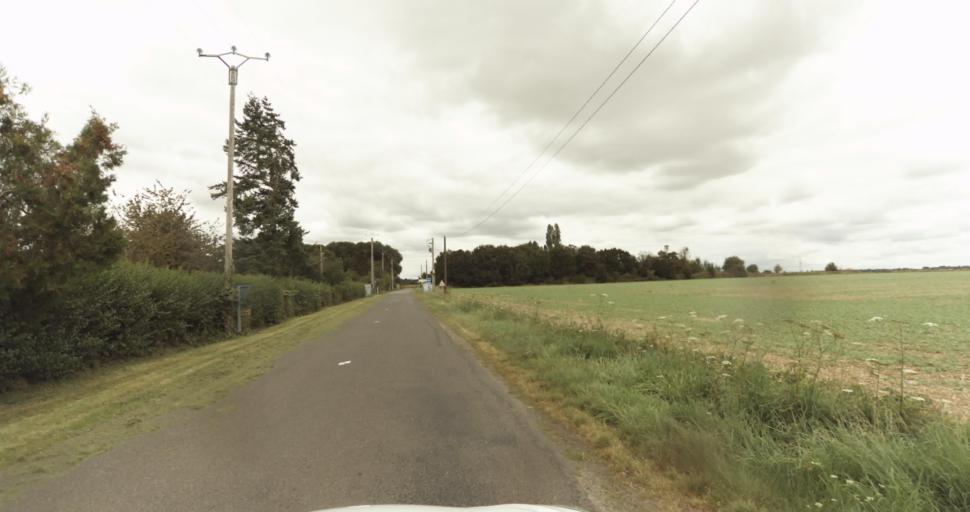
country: FR
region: Haute-Normandie
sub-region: Departement de l'Eure
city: La Madeleine-de-Nonancourt
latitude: 48.8312
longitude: 1.2262
